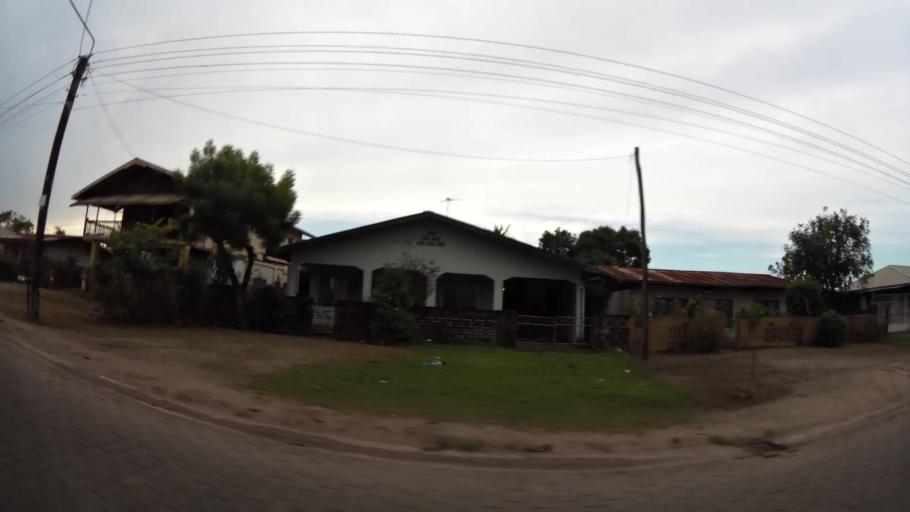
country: SR
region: Paramaribo
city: Paramaribo
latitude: 5.8044
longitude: -55.1909
